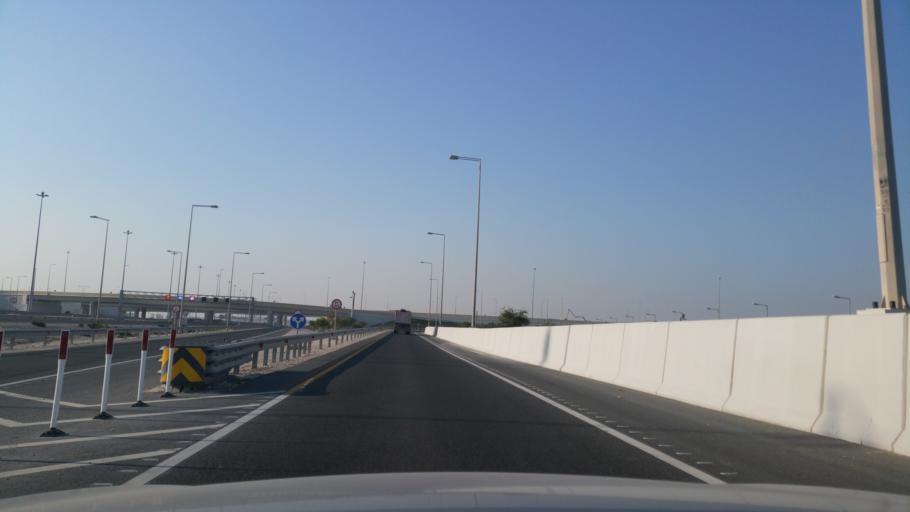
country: QA
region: Al Wakrah
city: Al Wukayr
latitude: 25.1596
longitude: 51.5703
